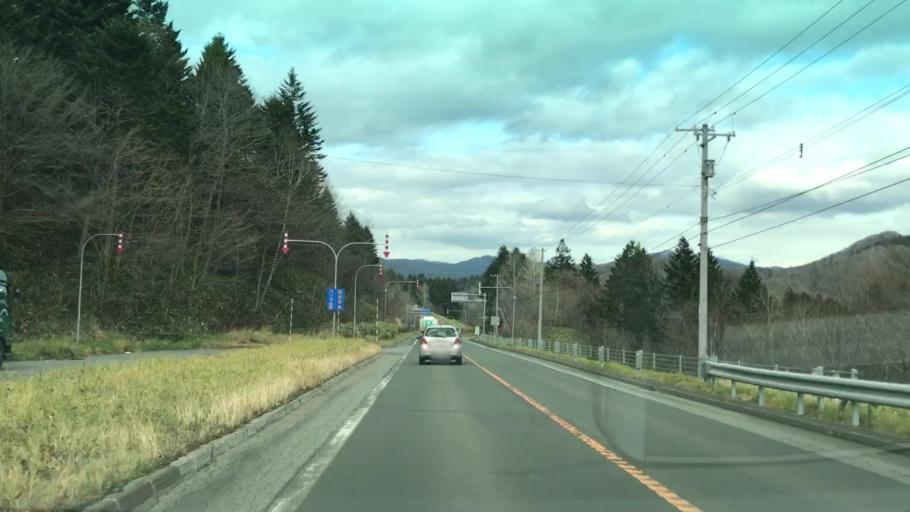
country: JP
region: Hokkaido
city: Shimo-furano
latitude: 42.9129
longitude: 142.4468
